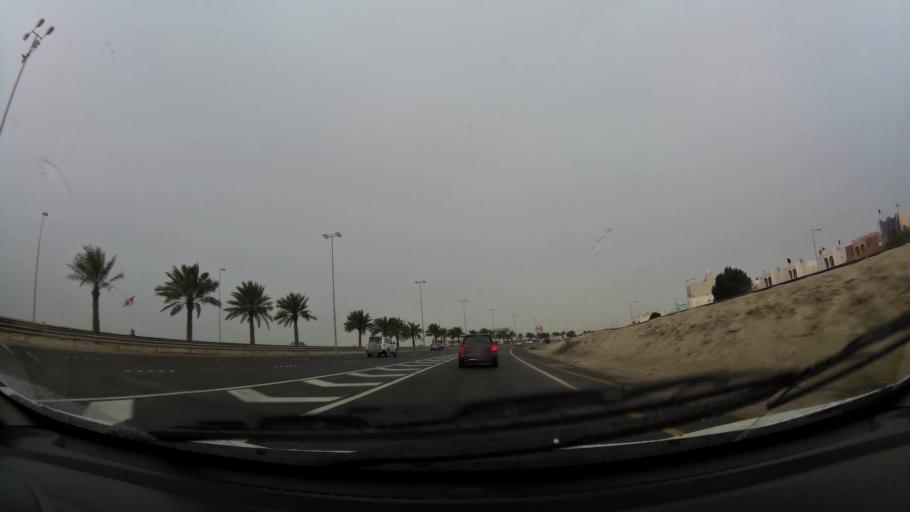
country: BH
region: Central Governorate
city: Madinat Hamad
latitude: 26.1174
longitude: 50.5101
